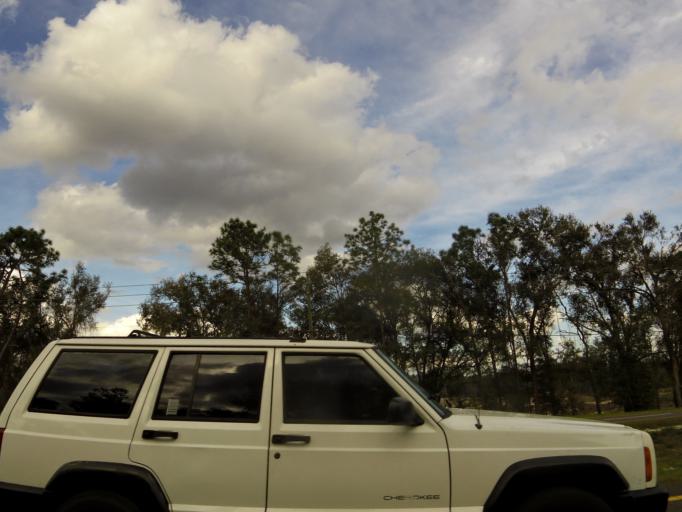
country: US
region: Florida
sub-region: Volusia County
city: Orange City
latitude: 28.9640
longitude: -81.2720
